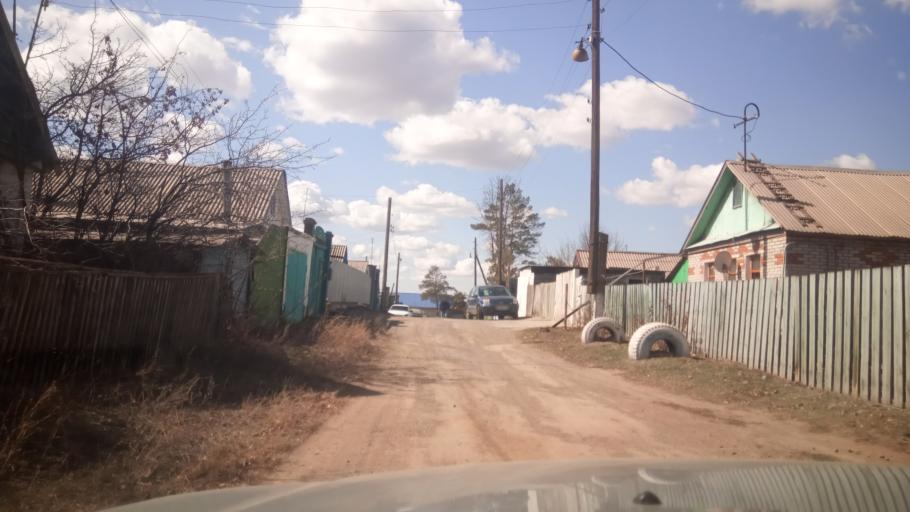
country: RU
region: Orenburg
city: Novotroitsk
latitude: 51.2101
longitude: 58.3165
